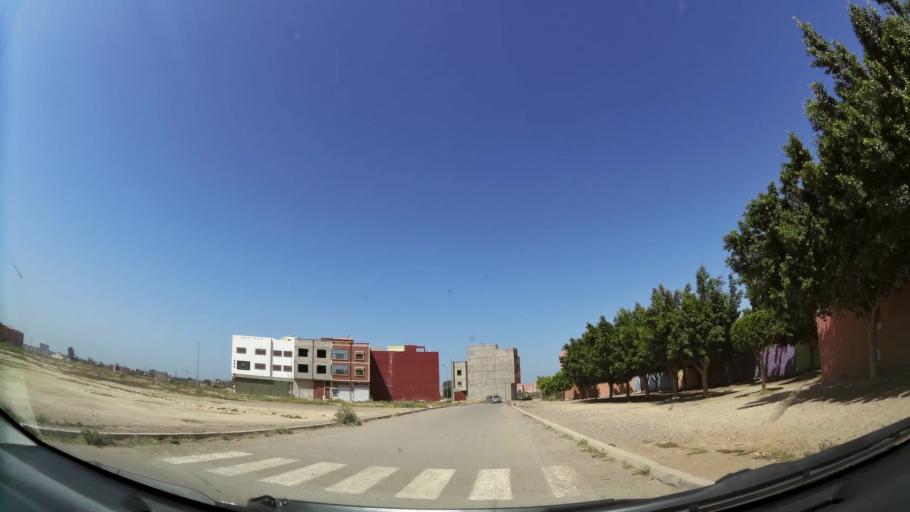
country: MA
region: Souss-Massa-Draa
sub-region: Inezgane-Ait Mellou
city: Inezgane
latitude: 30.3361
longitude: -9.5099
